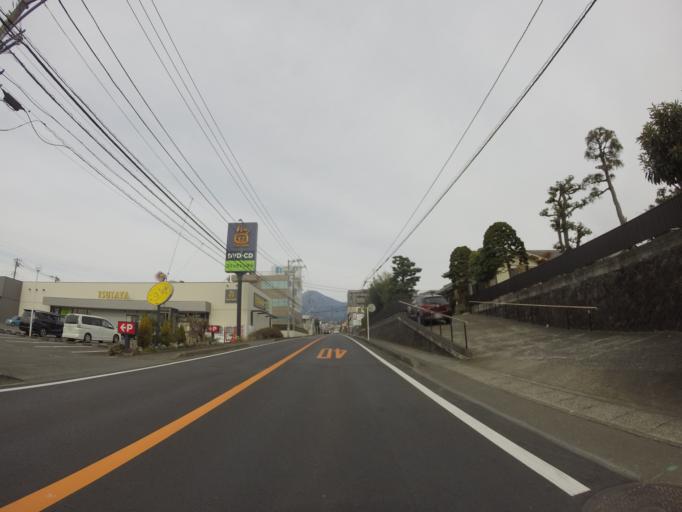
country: JP
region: Shizuoka
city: Fuji
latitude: 35.1716
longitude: 138.6812
